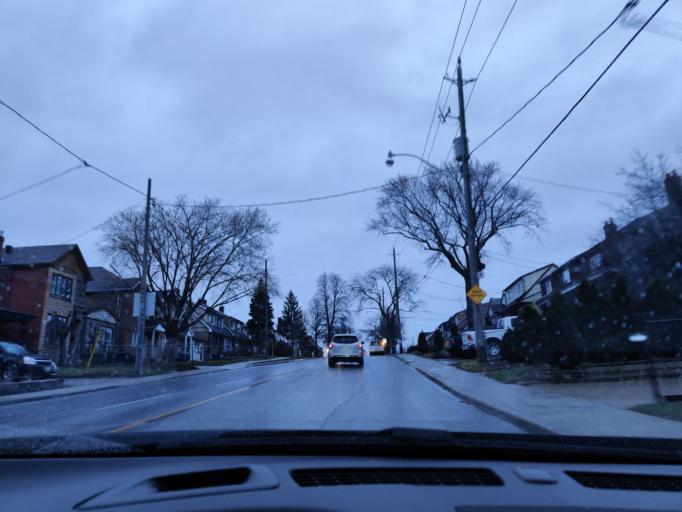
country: CA
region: Ontario
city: Toronto
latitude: 43.6828
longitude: -79.4579
